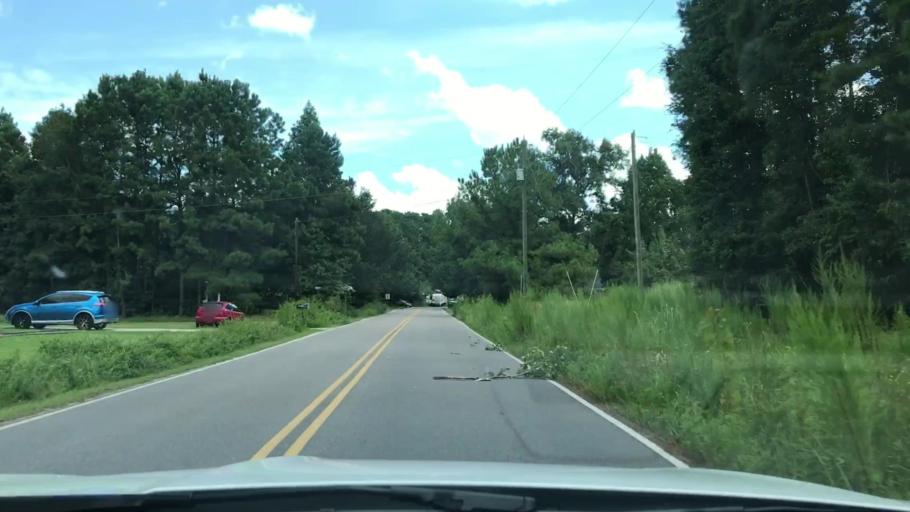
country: US
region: South Carolina
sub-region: Dorchester County
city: Summerville
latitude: 33.0335
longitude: -80.2107
